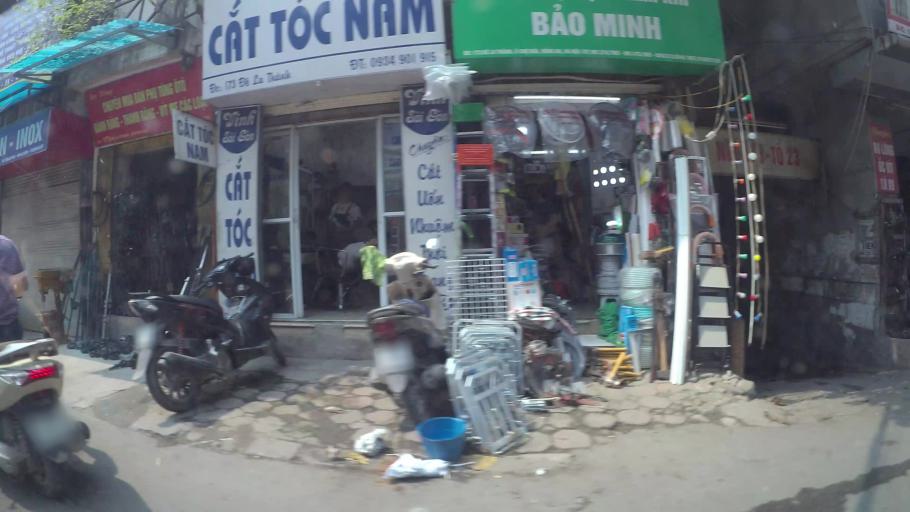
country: VN
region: Ha Noi
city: Dong Da
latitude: 21.0206
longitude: 105.8270
